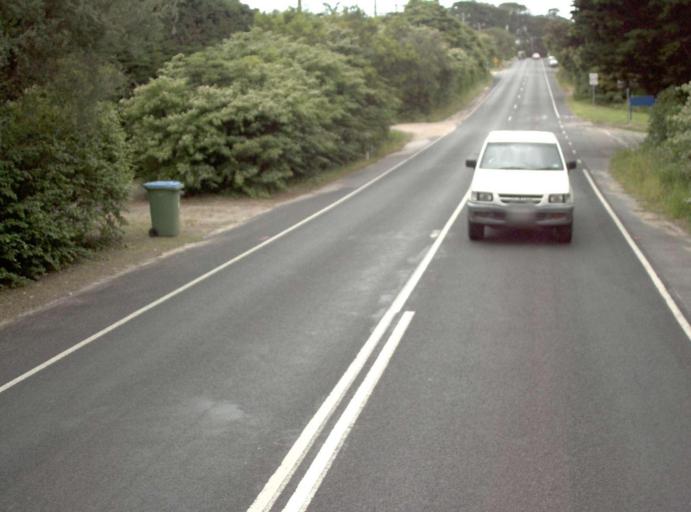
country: AU
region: Victoria
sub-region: Mornington Peninsula
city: Sorrento
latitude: -38.3256
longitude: 144.7347
